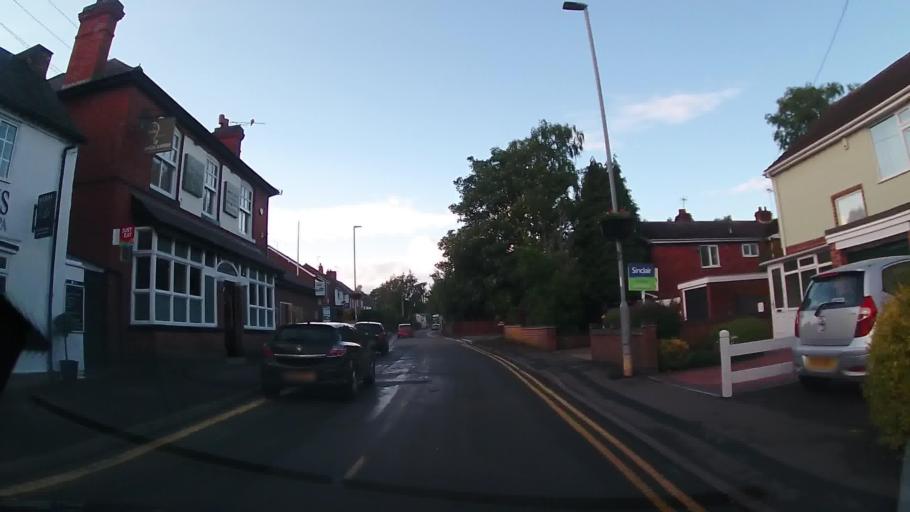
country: GB
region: England
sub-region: Leicestershire
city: Markfield
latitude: 52.6875
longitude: -1.2776
